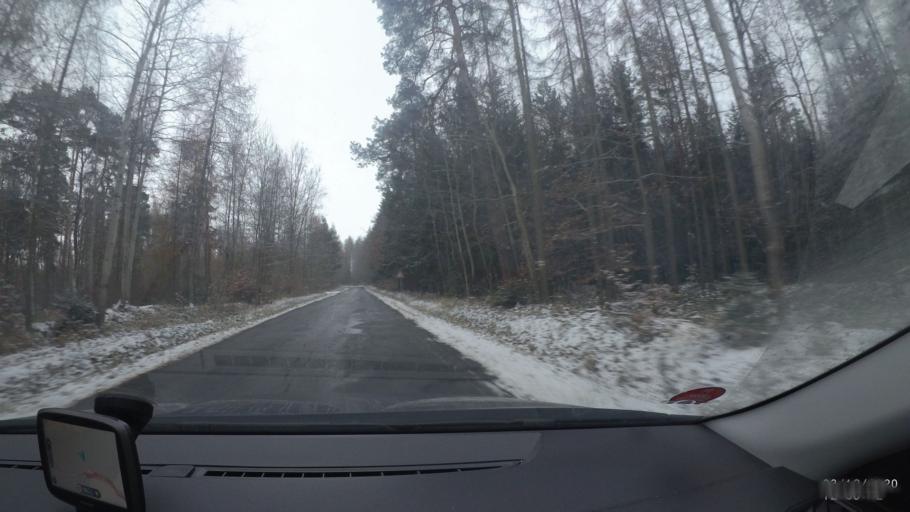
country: CZ
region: Central Bohemia
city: Nove Straseci
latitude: 50.1693
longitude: 13.8677
